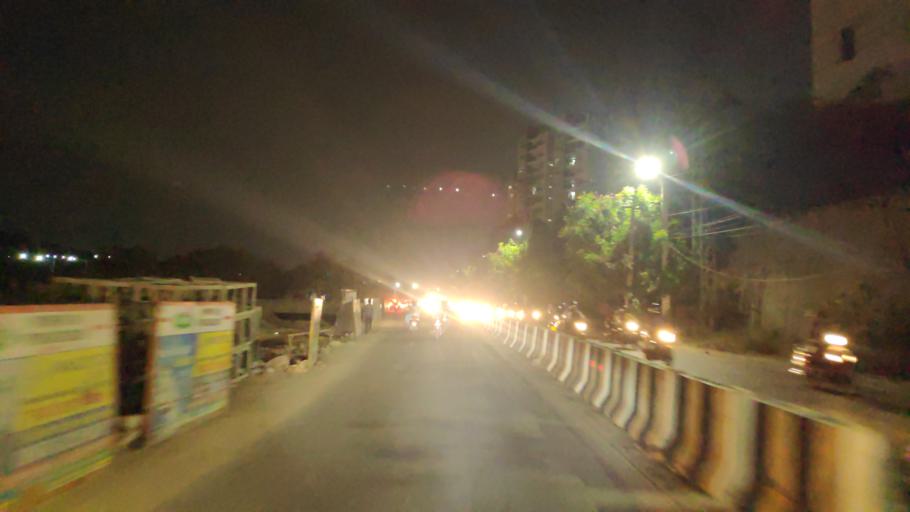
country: IN
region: Telangana
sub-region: Rangareddi
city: Kukatpalli
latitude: 17.4742
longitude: 78.3833
